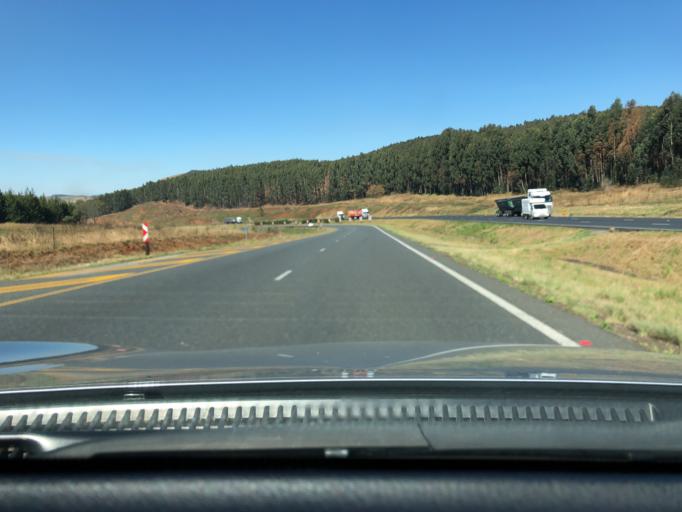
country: ZA
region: KwaZulu-Natal
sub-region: uMgungundlovu District Municipality
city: Howick
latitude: -29.3986
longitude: 30.1384
